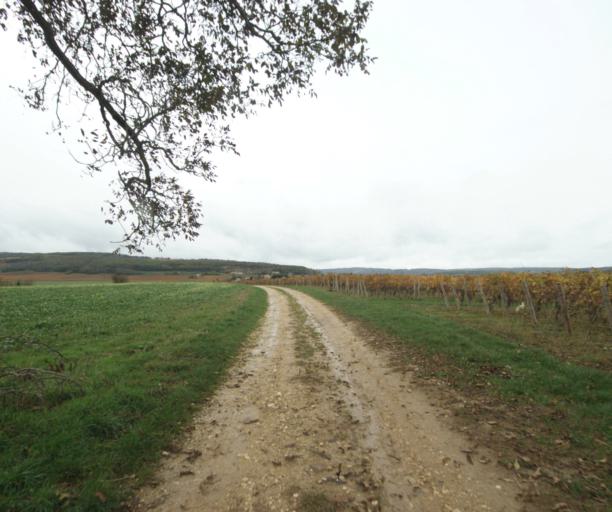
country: FR
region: Rhone-Alpes
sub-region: Departement de l'Ain
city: Pont-de-Vaux
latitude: 46.4684
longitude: 4.8639
